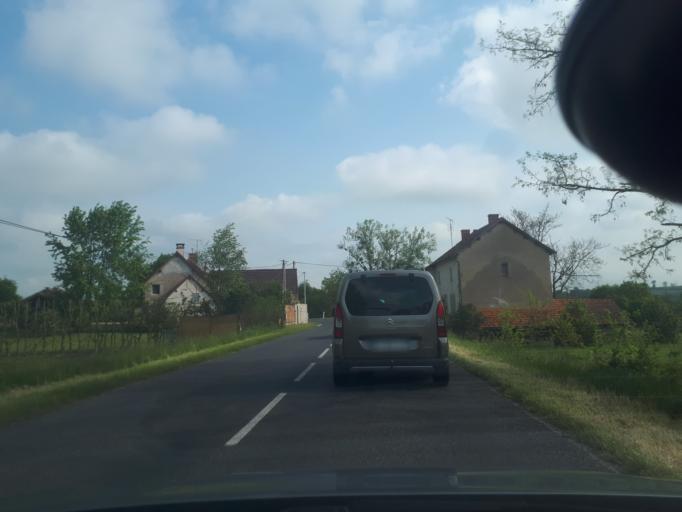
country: FR
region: Auvergne
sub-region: Departement de l'Allier
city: Lapalisse
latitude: 46.3365
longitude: 3.5812
